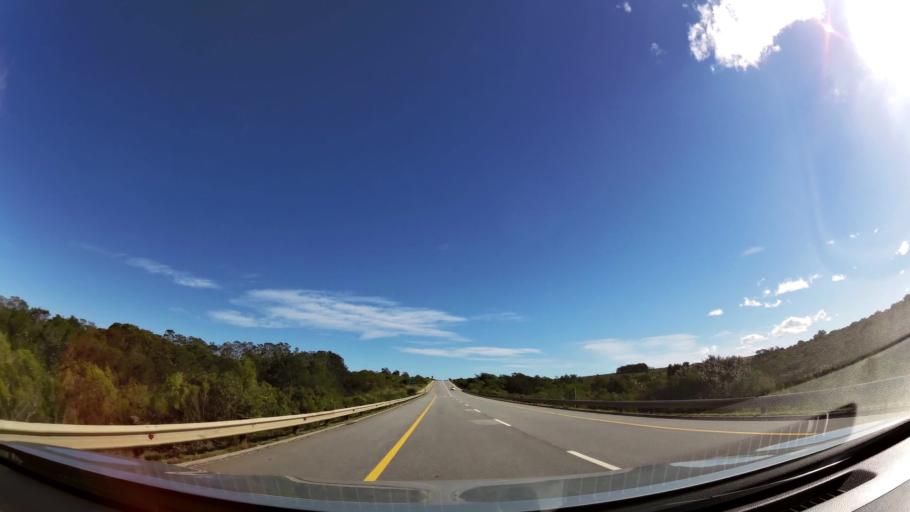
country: ZA
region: Eastern Cape
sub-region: Cacadu District Municipality
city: Kruisfontein
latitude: -34.0077
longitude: 24.6677
